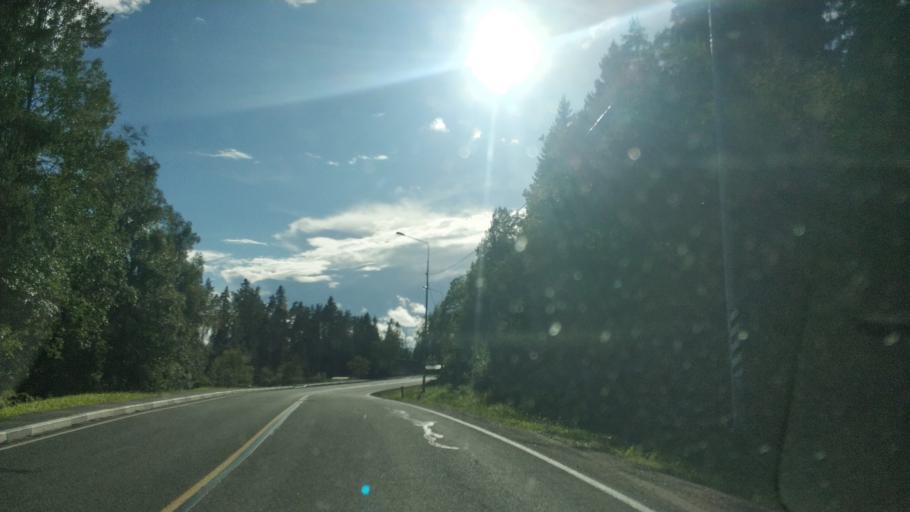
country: RU
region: Republic of Karelia
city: Lakhdenpokh'ya
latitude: 61.5371
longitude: 30.2235
